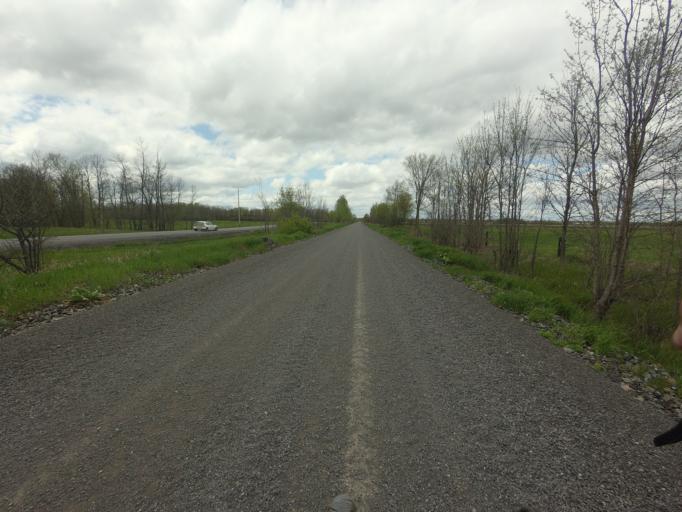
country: CA
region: Ontario
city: Carleton Place
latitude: 45.2719
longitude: -76.2371
